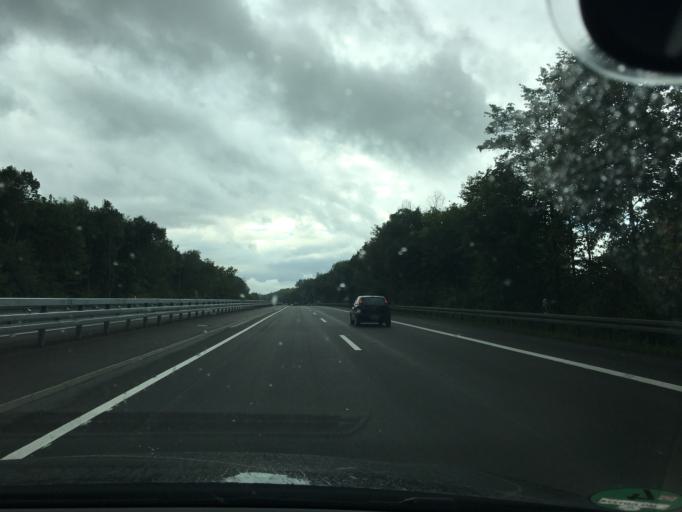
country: DE
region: North Rhine-Westphalia
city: Bruhl
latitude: 50.7978
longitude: 6.8857
